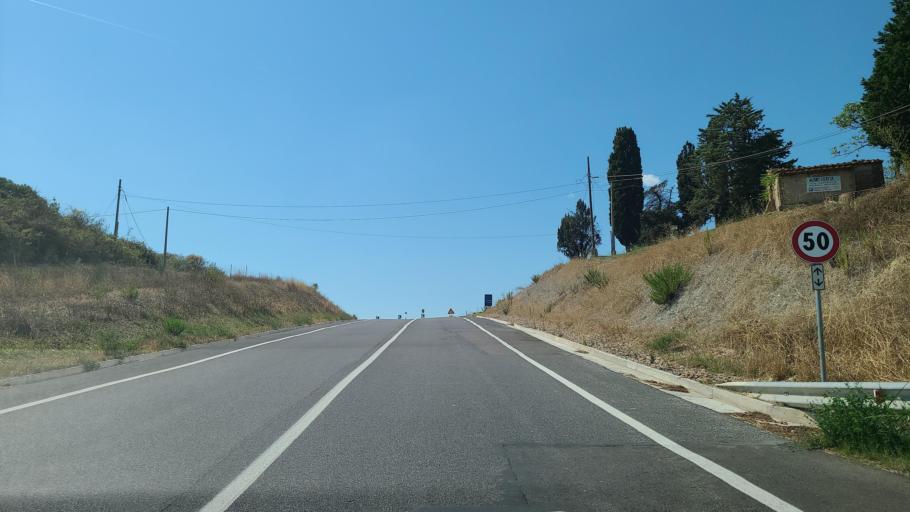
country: IT
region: Tuscany
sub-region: Province of Pisa
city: Volterra
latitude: 43.3827
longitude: 10.9295
